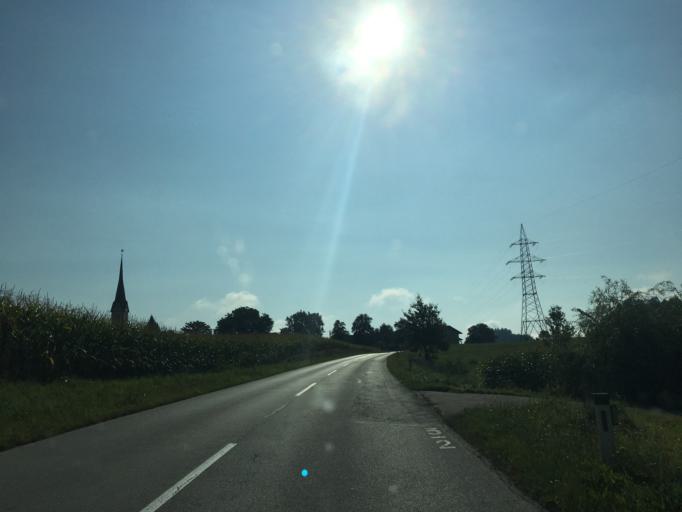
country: AT
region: Carinthia
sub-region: Politischer Bezirk Volkermarkt
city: Voelkermarkt
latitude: 46.6914
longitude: 14.6311
